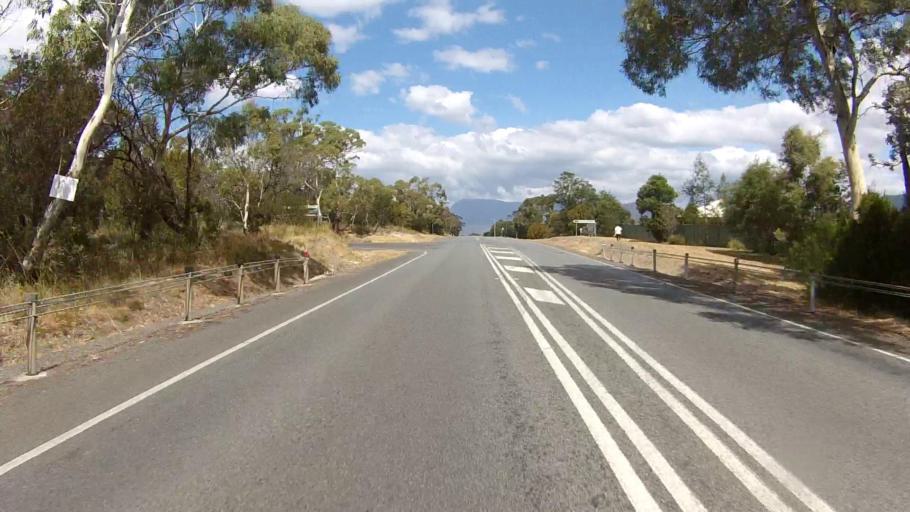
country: AU
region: Tasmania
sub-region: Brighton
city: Old Beach
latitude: -42.7690
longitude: 147.2695
